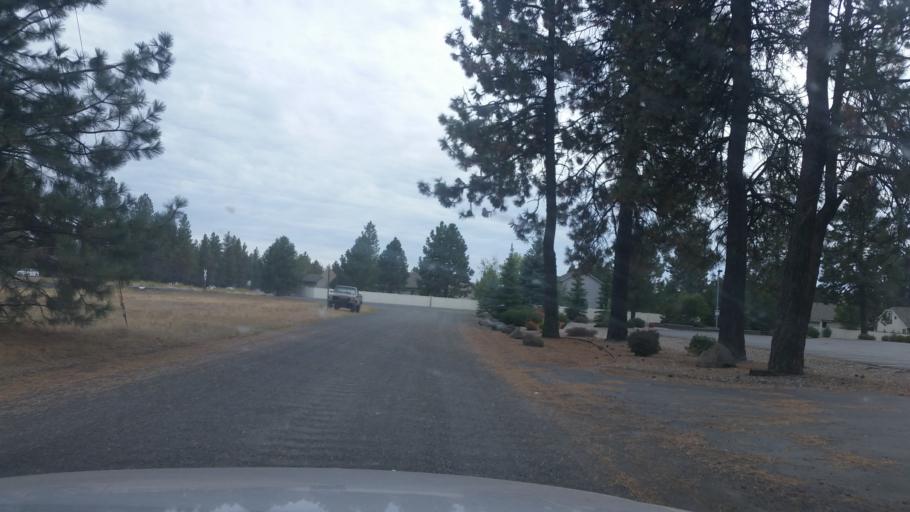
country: US
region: Washington
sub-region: Spokane County
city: Cheney
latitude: 47.5146
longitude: -117.5654
